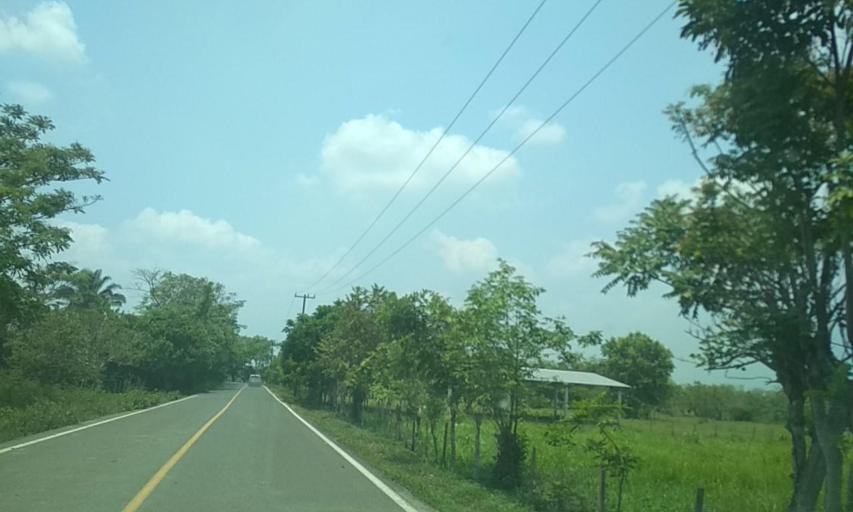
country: MX
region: Tabasco
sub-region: Huimanguillo
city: Francisco Rueda
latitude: 17.7593
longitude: -94.0092
